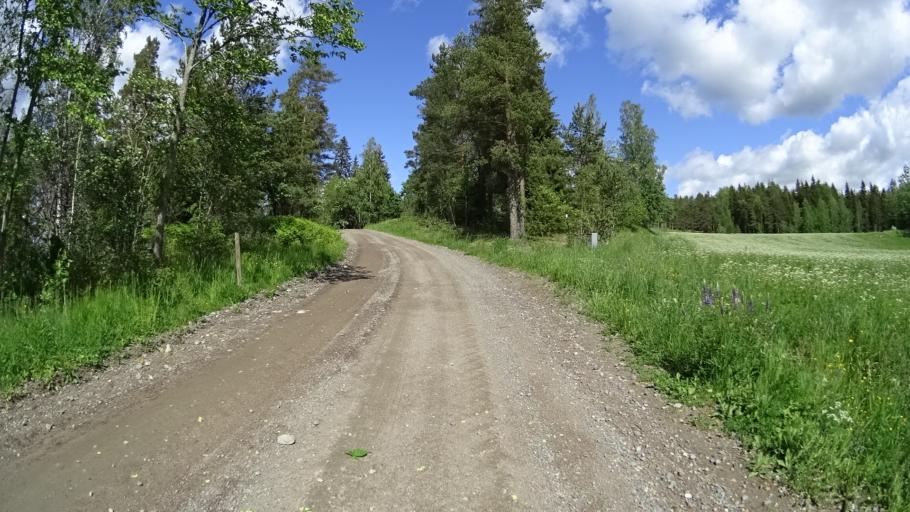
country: FI
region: Uusimaa
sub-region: Raaseporin
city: Karis
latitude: 60.1293
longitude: 23.6167
